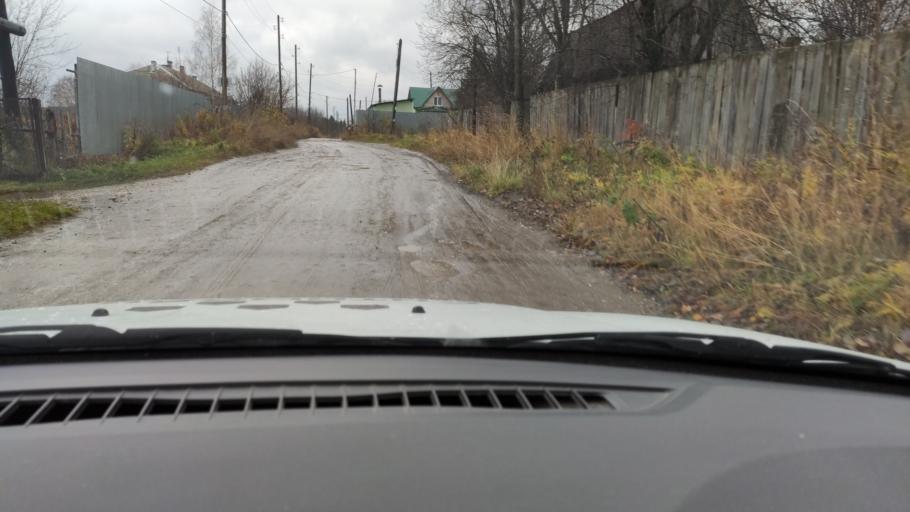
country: RU
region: Perm
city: Sylva
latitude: 58.0472
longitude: 56.7359
